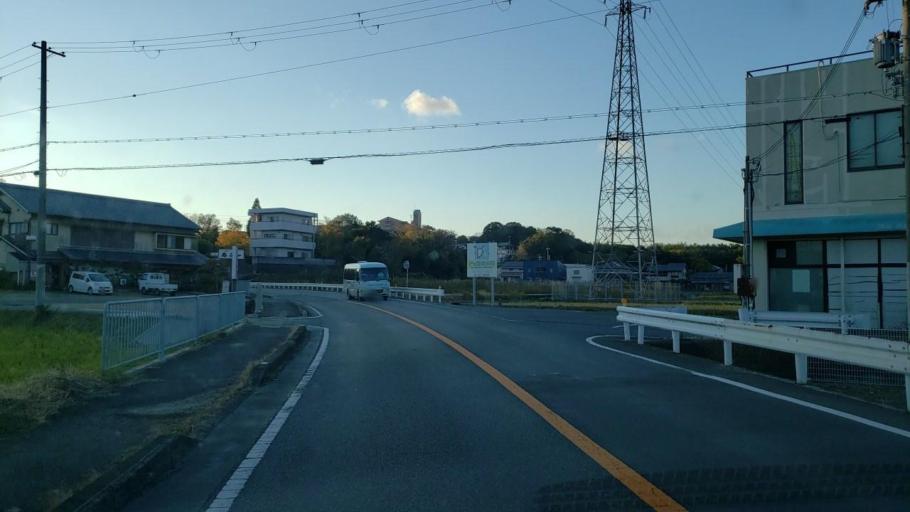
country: JP
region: Hyogo
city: Sumoto
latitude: 34.4413
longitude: 134.8927
